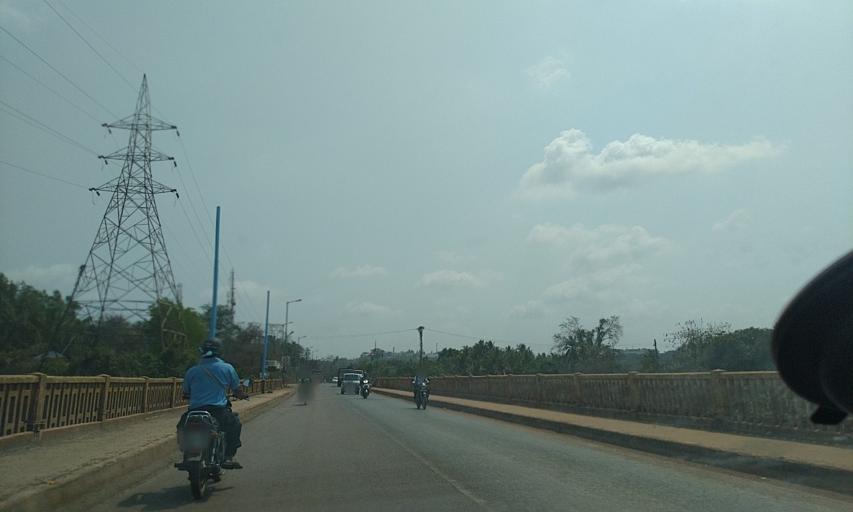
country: IN
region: Goa
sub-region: North Goa
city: Colovale
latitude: 15.6486
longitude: 73.8362
